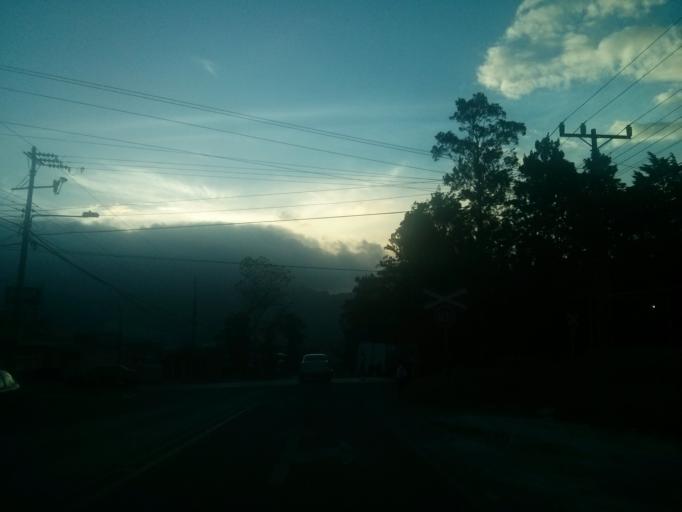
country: CR
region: Cartago
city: Cartago
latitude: 9.8785
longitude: -83.9297
